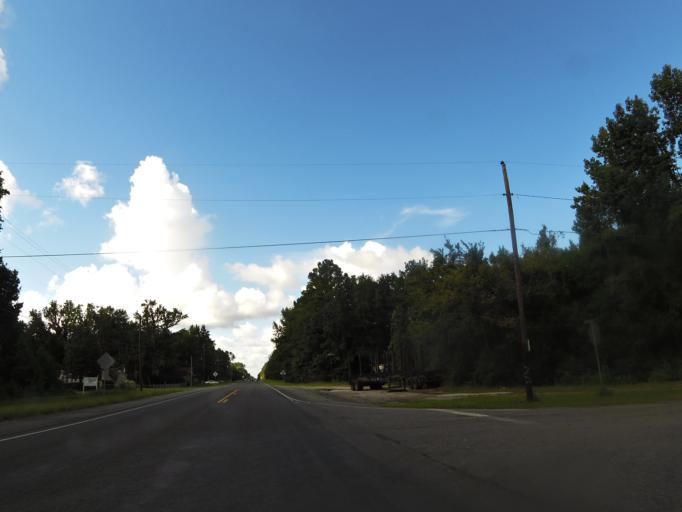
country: US
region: Georgia
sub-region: Camden County
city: Woodbine
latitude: 30.9321
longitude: -81.7164
